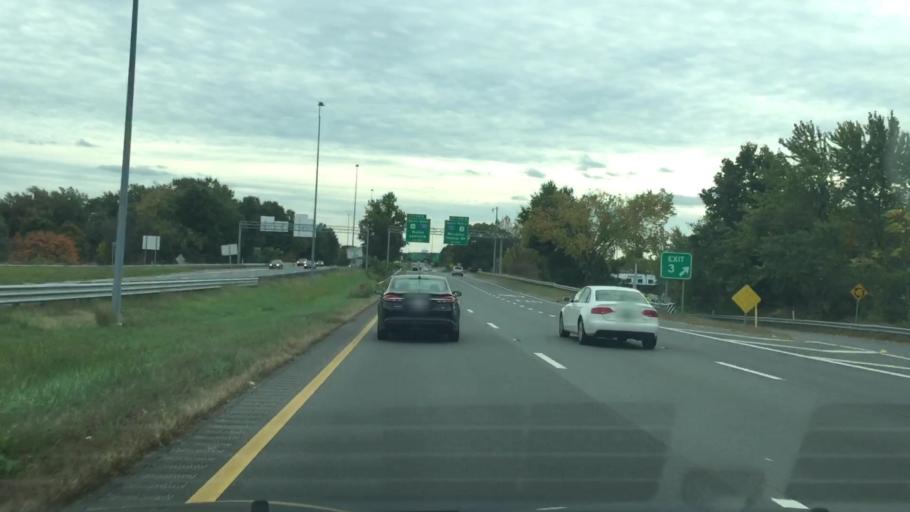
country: US
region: Massachusetts
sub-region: Middlesex County
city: Lowell
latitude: 42.6202
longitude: -71.3203
